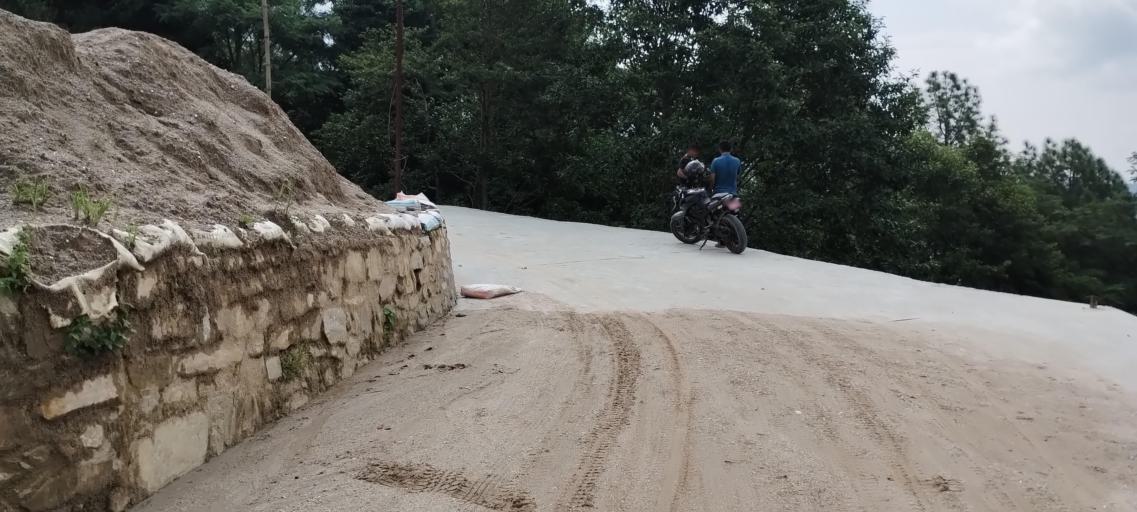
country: NP
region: Central Region
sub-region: Bagmati Zone
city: Kathmandu
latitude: 27.7868
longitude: 85.3604
